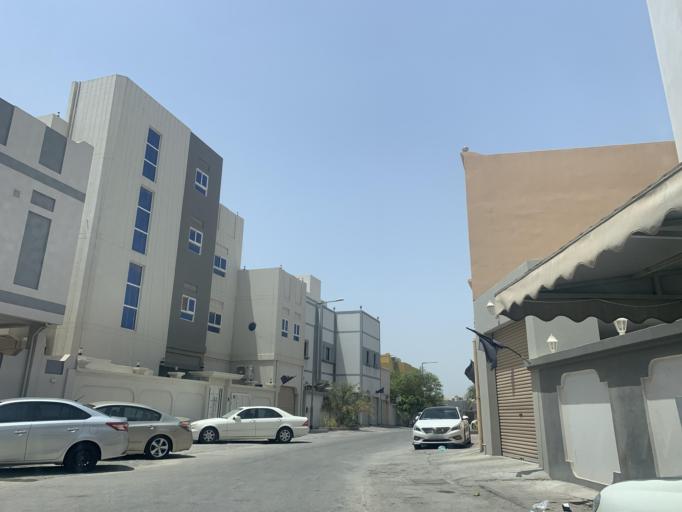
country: BH
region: Central Governorate
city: Madinat Hamad
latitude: 26.1448
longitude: 50.5036
